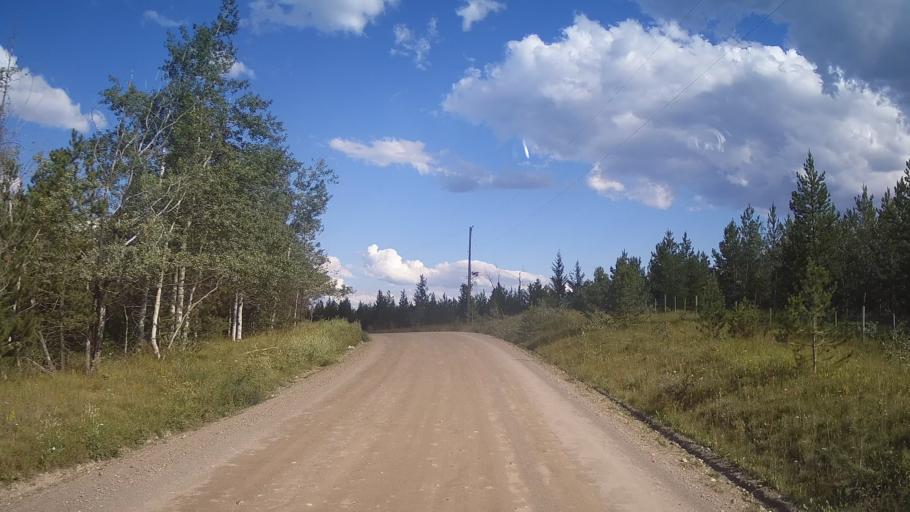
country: CA
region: British Columbia
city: Cache Creek
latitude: 51.2715
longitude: -121.7264
